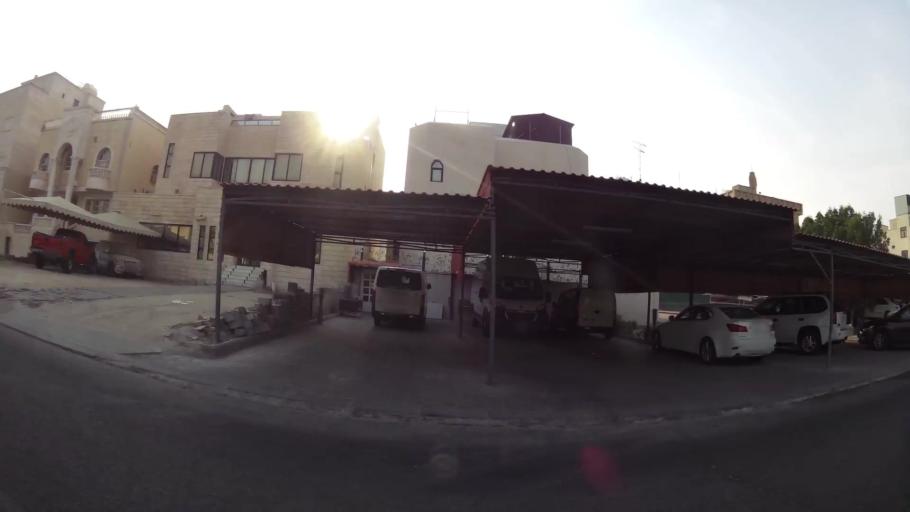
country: KW
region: Mubarak al Kabir
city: Mubarak al Kabir
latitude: 29.1888
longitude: 48.0709
